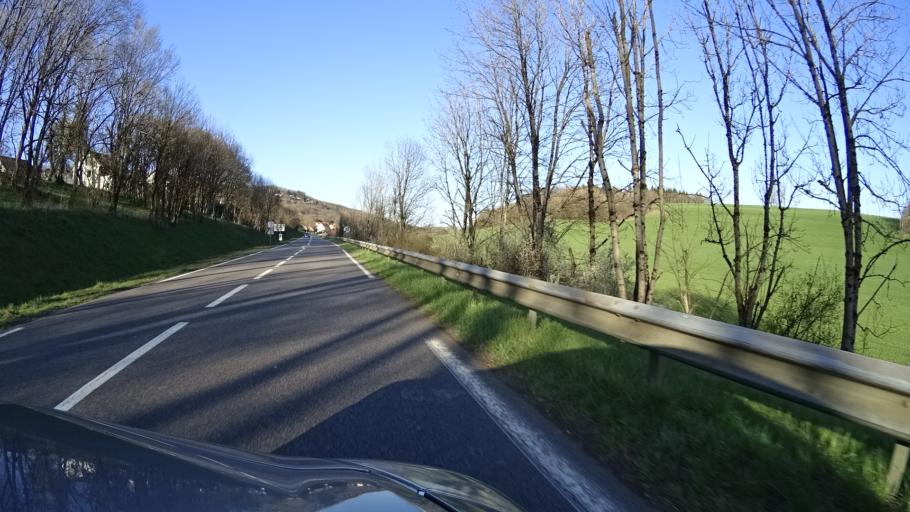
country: FR
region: Franche-Comte
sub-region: Departement du Doubs
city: Beure
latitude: 47.1973
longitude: 6.0271
